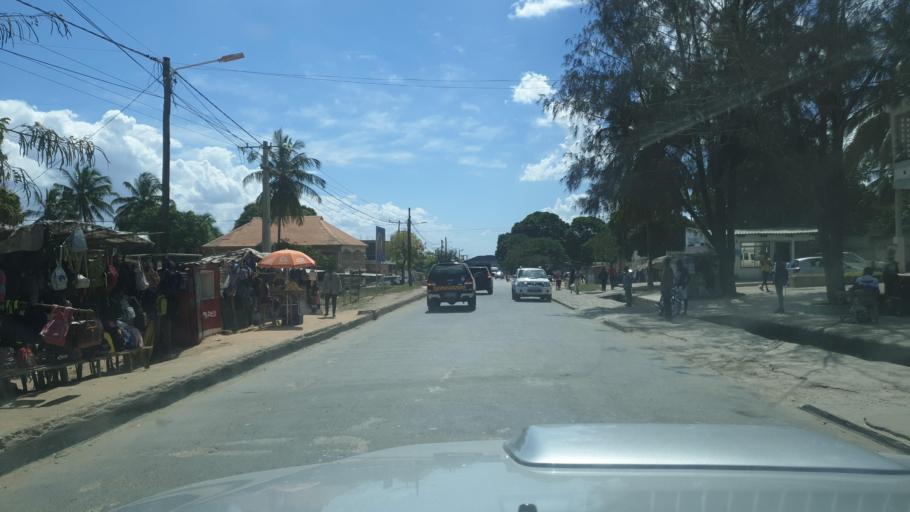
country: MZ
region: Nampula
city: Nacala
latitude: -14.5539
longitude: 40.6854
